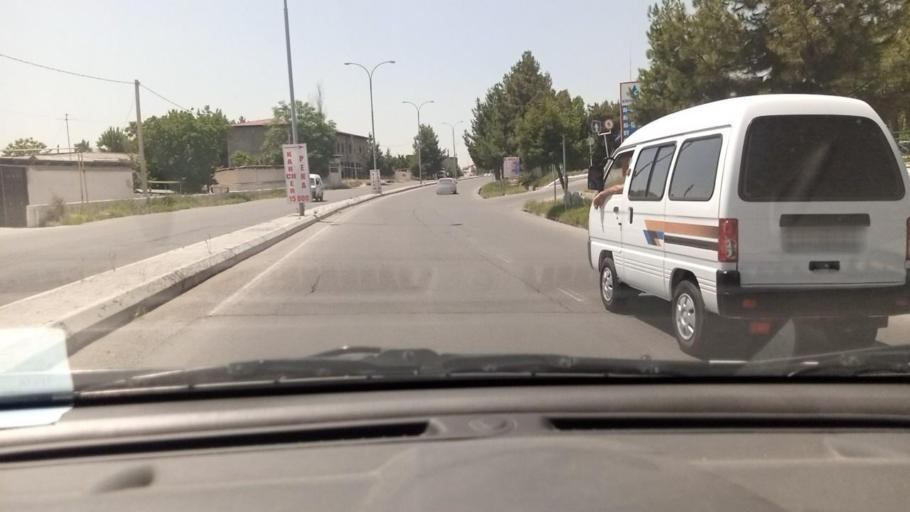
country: UZ
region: Toshkent Shahri
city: Tashkent
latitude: 41.2479
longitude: 69.2083
